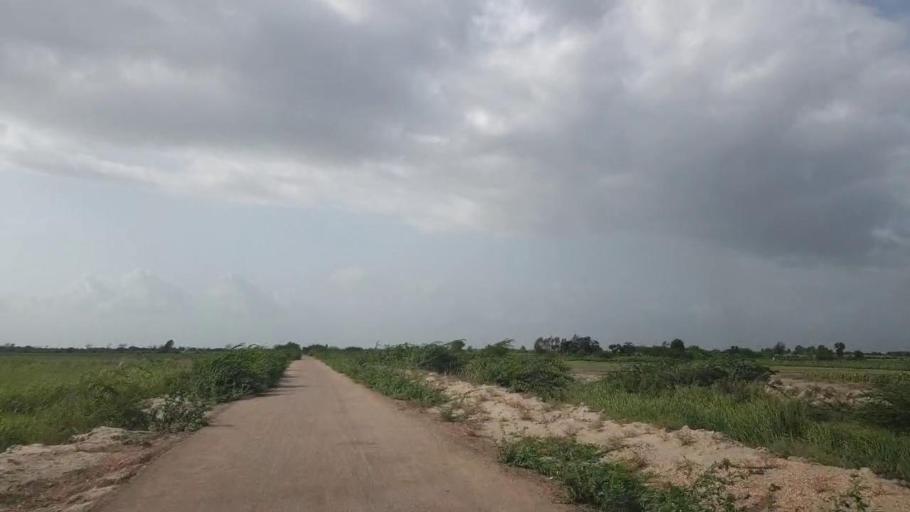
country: PK
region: Sindh
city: Kadhan
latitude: 24.5725
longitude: 69.0611
